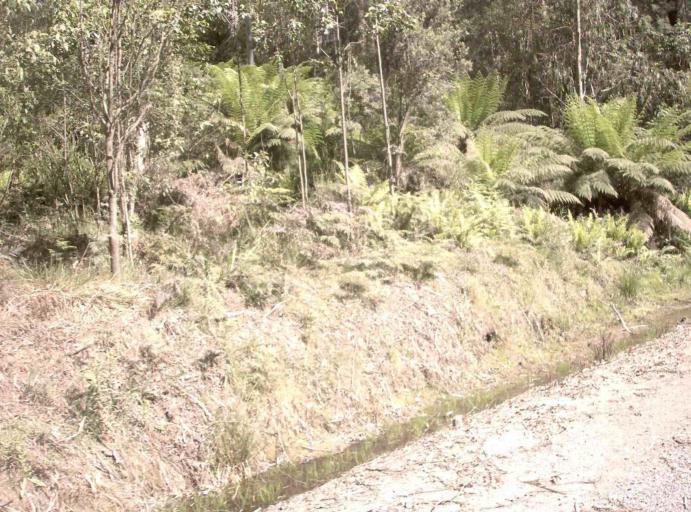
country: AU
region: New South Wales
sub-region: Bombala
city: Bombala
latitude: -37.2238
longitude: 148.7479
